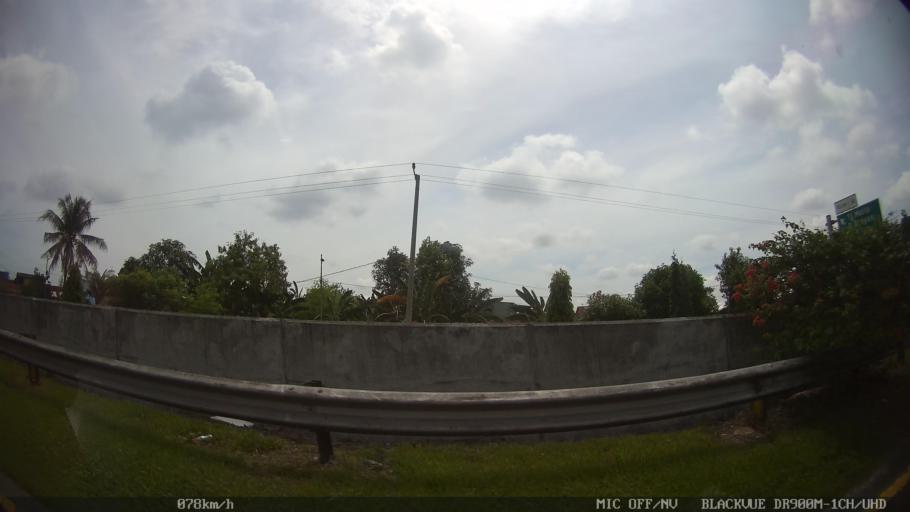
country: ID
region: North Sumatra
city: Labuhan Deli
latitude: 3.6614
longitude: 98.6824
